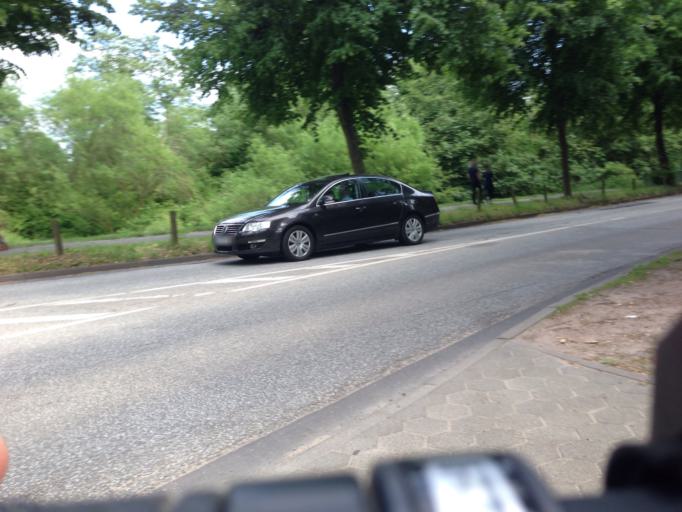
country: DE
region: Hamburg
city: Farmsen-Berne
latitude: 53.5934
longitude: 10.1220
